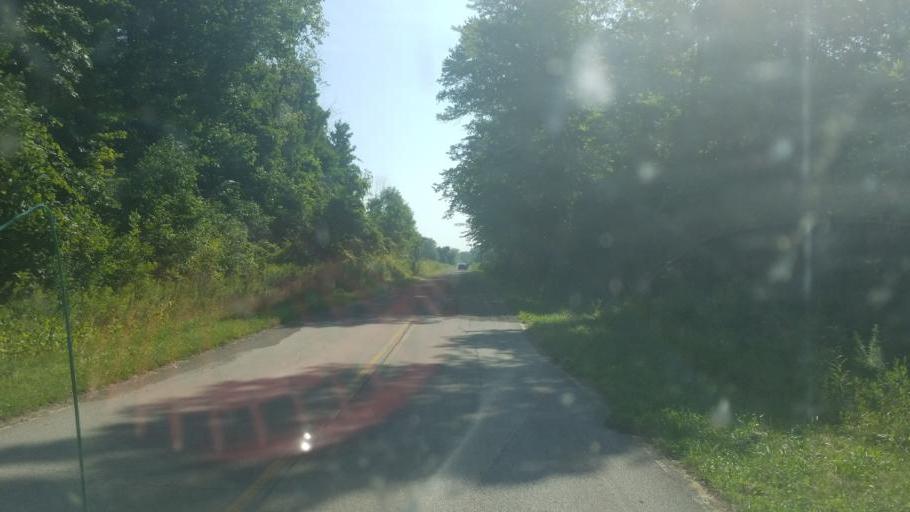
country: US
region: Ohio
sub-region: Wayne County
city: West Salem
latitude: 41.0424
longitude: -82.1920
